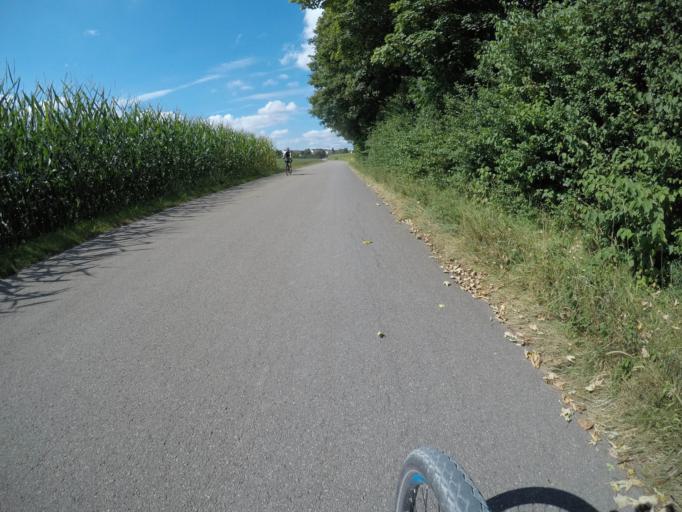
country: DE
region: Bavaria
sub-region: Swabia
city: Wittislingen
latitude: 48.6137
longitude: 10.4251
